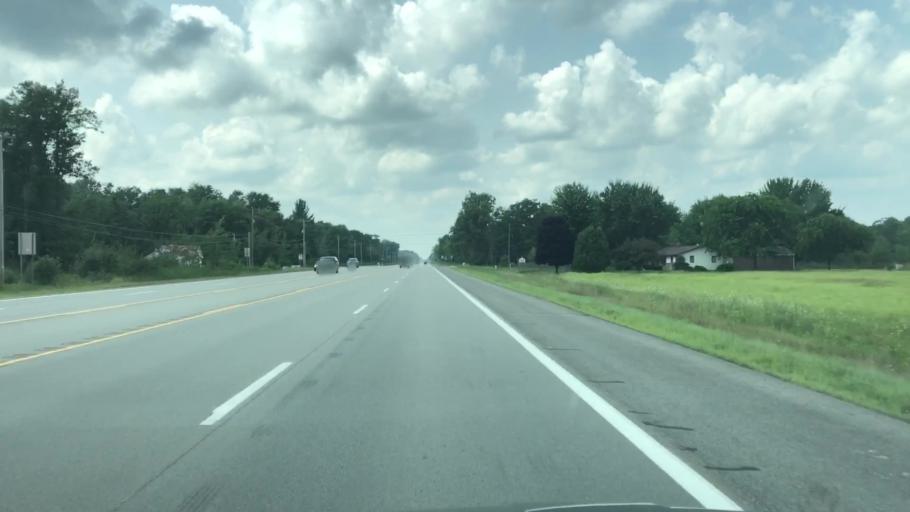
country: US
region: Michigan
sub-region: Midland County
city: Coleman
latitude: 43.6113
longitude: -84.4666
